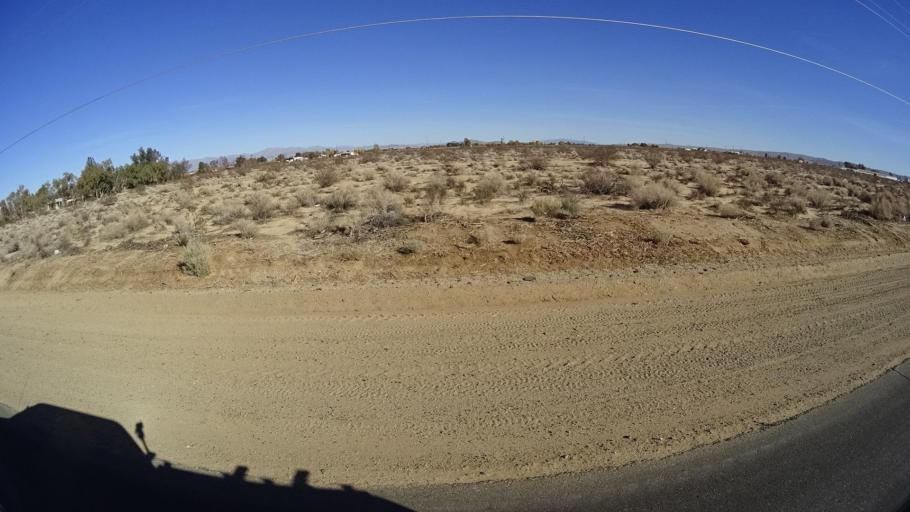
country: US
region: California
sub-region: Kern County
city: Inyokern
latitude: 35.6361
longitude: -117.8093
